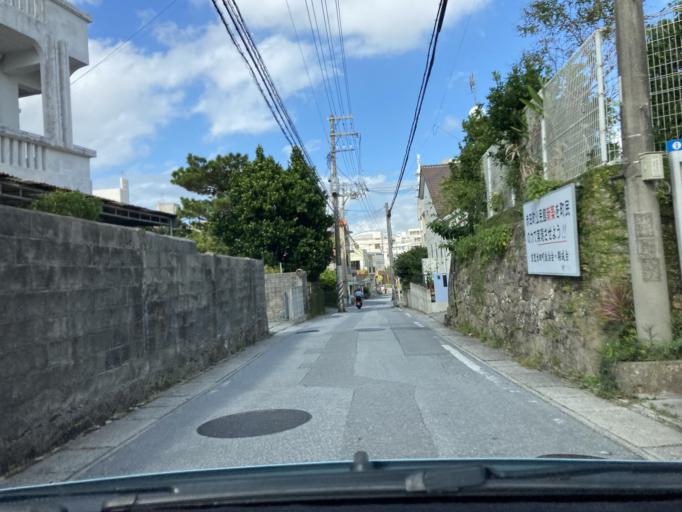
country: JP
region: Okinawa
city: Naha-shi
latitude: 26.2166
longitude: 127.7229
